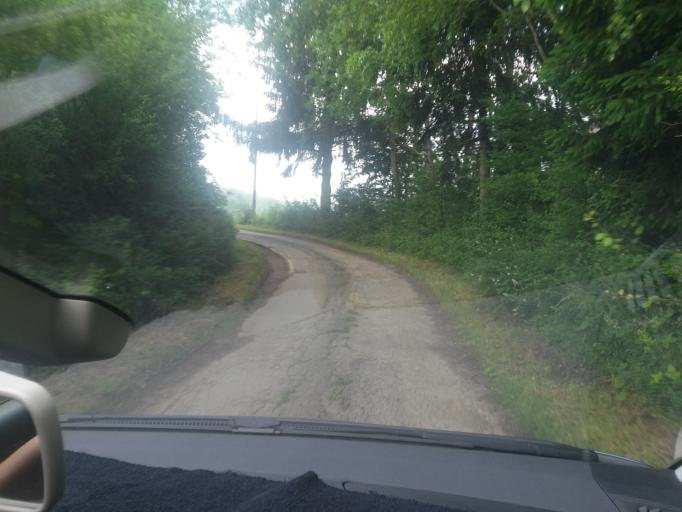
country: BE
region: Wallonia
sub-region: Province du Luxembourg
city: Arlon
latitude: 49.6915
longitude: 5.7529
